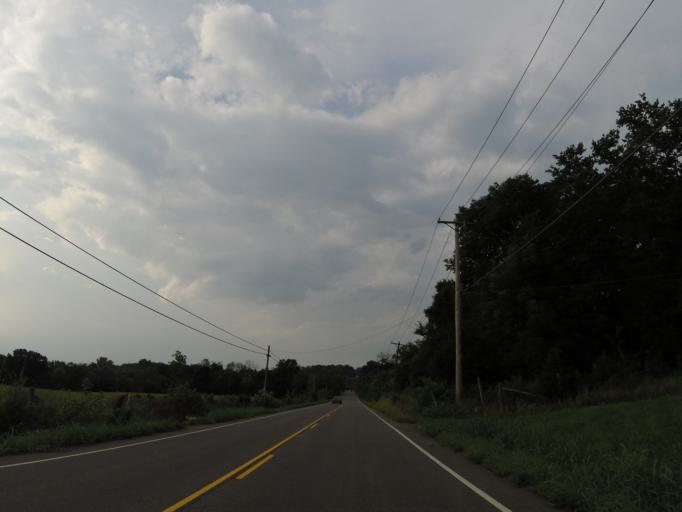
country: US
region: Tennessee
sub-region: Blount County
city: Eagleton Village
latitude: 35.8417
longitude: -83.9412
